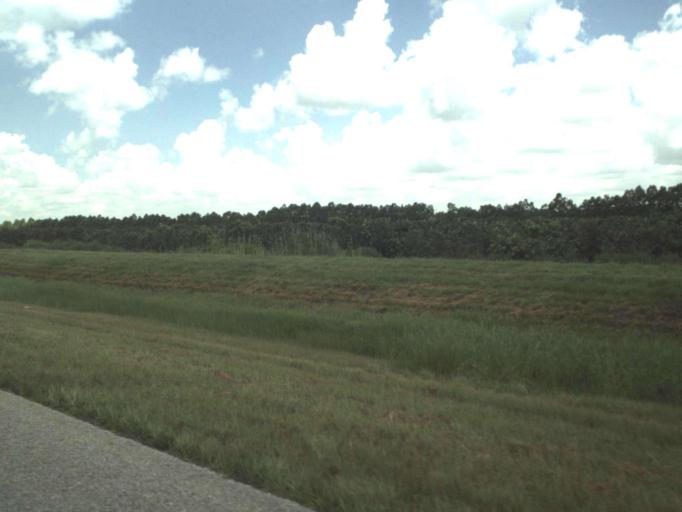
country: US
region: Florida
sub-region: Indian River County
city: West Vero Corridor
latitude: 27.6402
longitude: -80.6022
